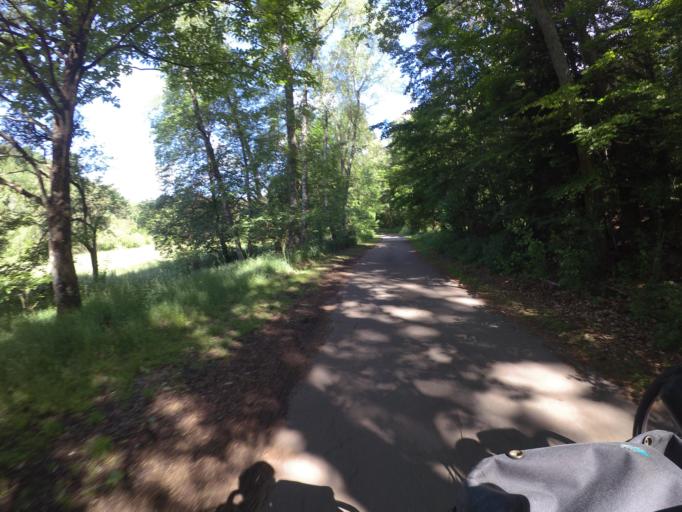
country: DE
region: Rheinland-Pfalz
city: Fischbach
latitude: 49.0950
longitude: 7.7085
